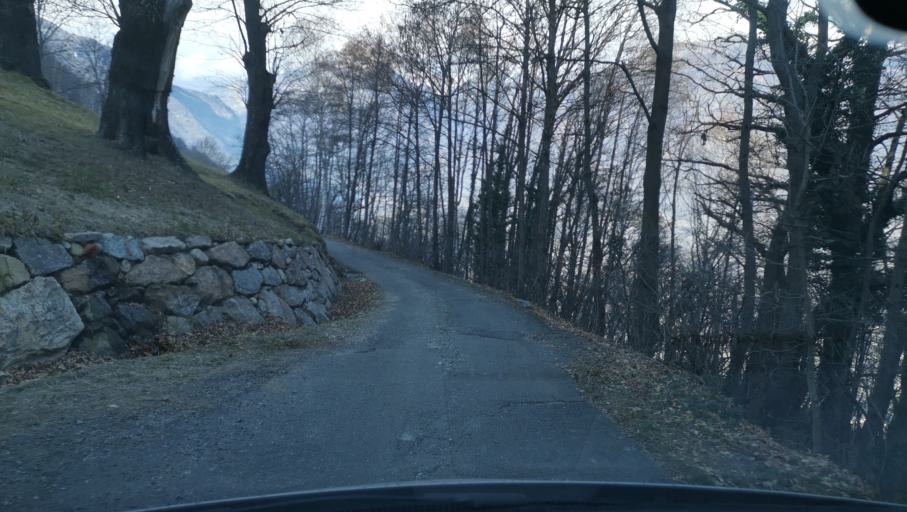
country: IT
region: Piedmont
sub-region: Provincia di Torino
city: Tavagnasco
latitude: 45.5365
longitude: 7.8174
